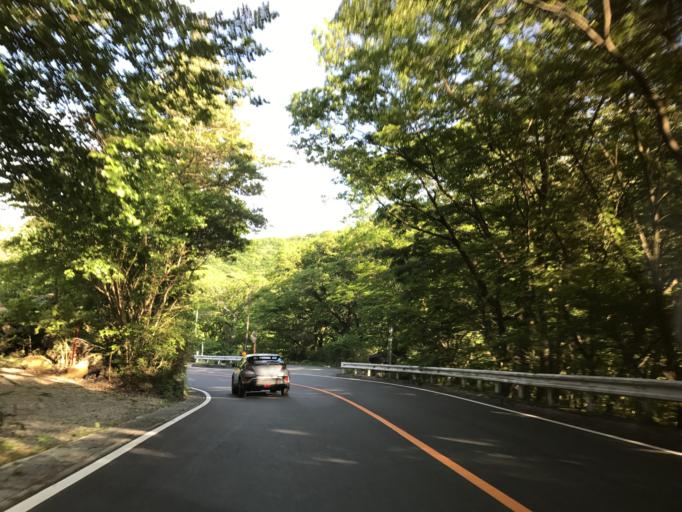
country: JP
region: Kanagawa
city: Hakone
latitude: 35.2592
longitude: 139.0337
